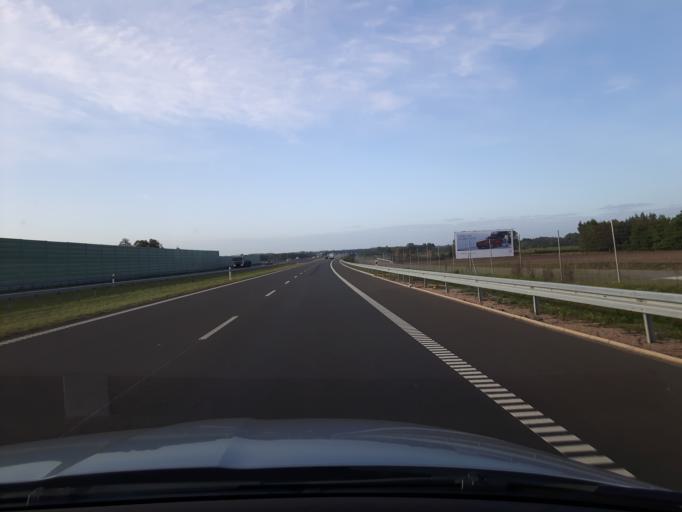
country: PL
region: Masovian Voivodeship
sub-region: Powiat radomski
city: Jedlinsk
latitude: 51.5065
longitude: 21.0814
